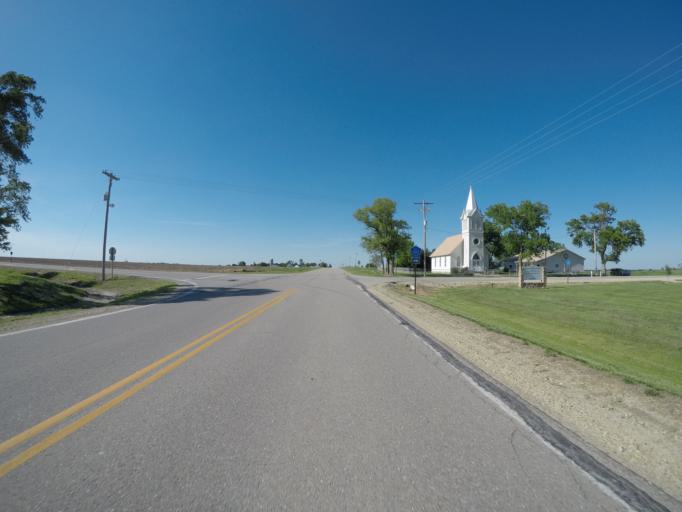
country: US
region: Kansas
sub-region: Riley County
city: Fort Riley North
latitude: 39.3349
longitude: -96.8307
